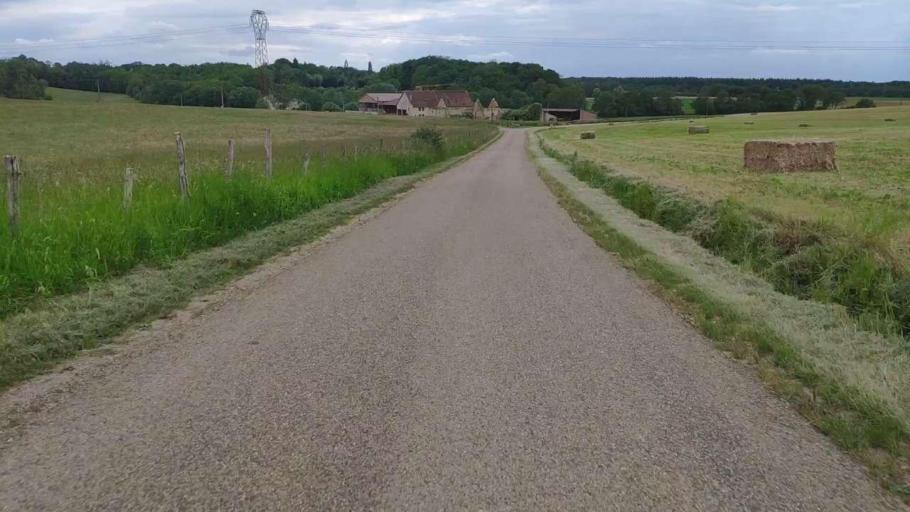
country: FR
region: Franche-Comte
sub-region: Departement du Jura
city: Bletterans
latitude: 46.7996
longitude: 5.5479
